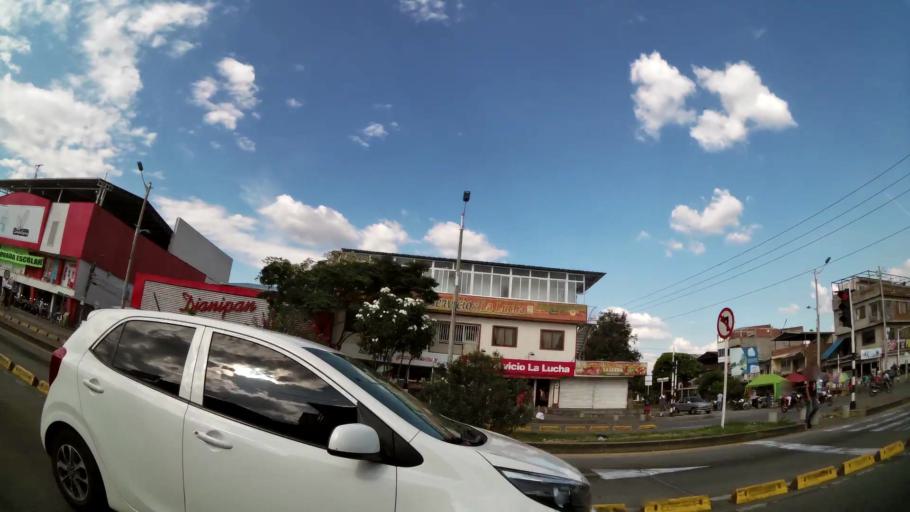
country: CO
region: Valle del Cauca
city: Cali
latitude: 3.4256
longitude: -76.4950
